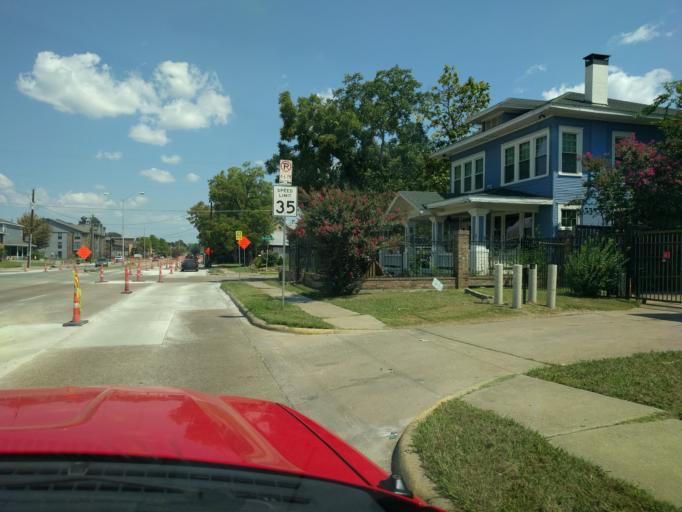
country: US
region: Texas
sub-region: Dallas County
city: Highland Park
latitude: 32.7974
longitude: -96.7607
